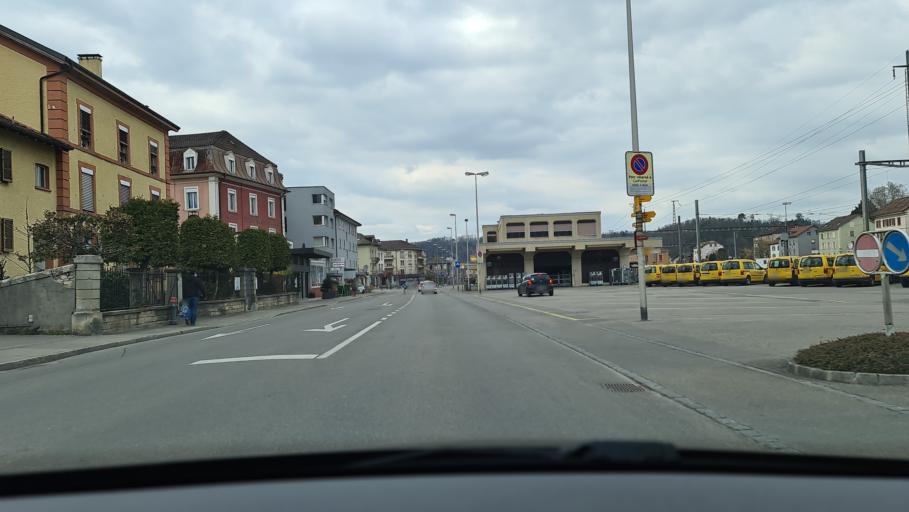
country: CH
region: Jura
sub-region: Porrentruy District
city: Porrentruy
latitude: 47.4192
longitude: 7.0794
